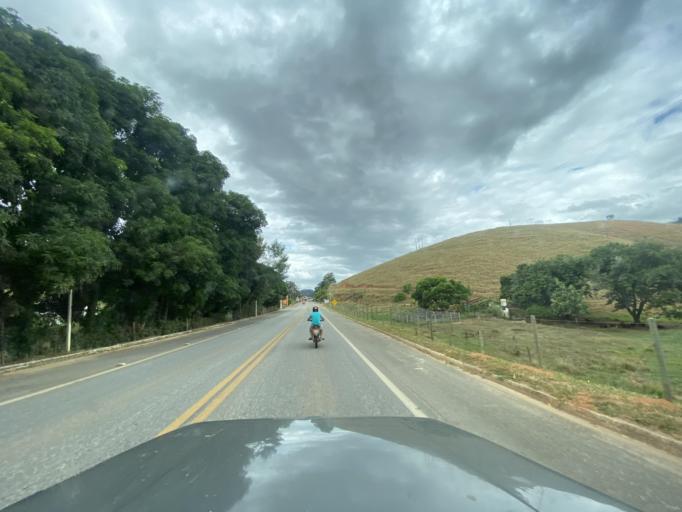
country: BR
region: Espirito Santo
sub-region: Alegre
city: Alegre
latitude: -20.7516
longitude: -41.4640
